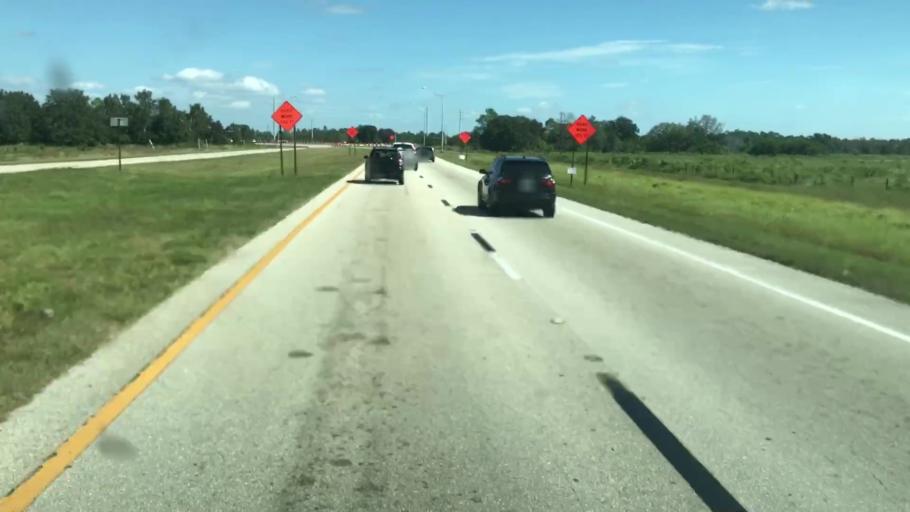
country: US
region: Florida
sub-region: Lee County
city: Gateway
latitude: 26.5778
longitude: -81.7185
